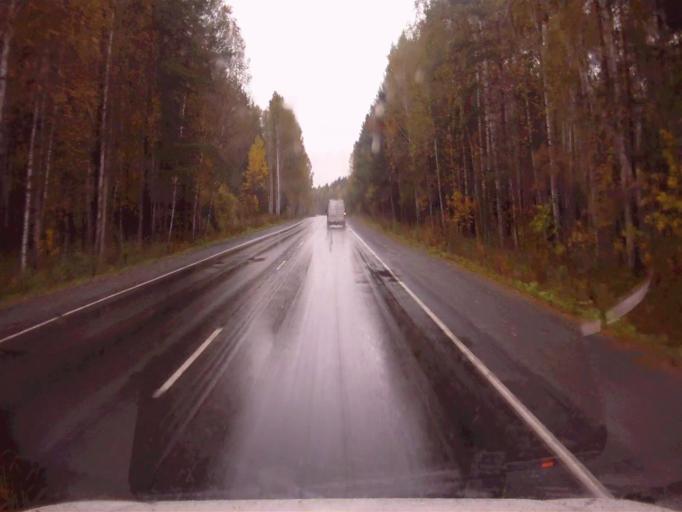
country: RU
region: Chelyabinsk
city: Tayginka
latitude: 55.5650
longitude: 60.6495
